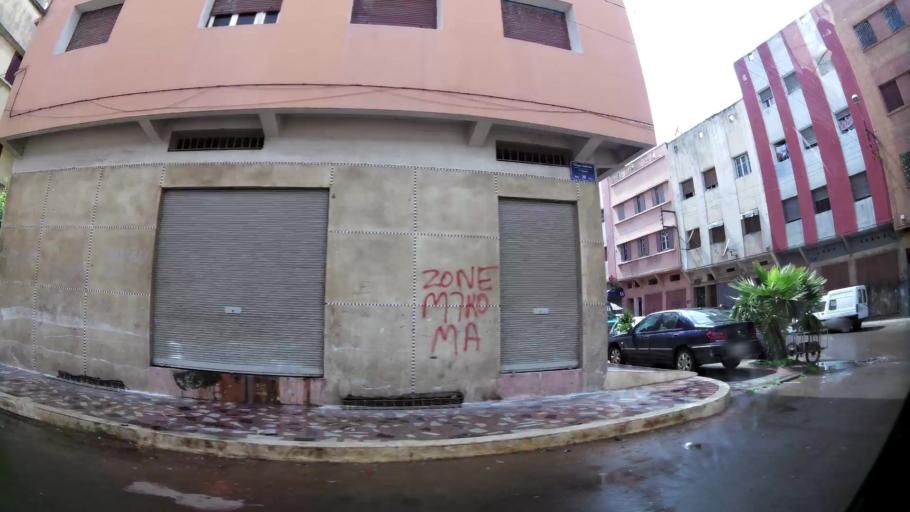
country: MA
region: Grand Casablanca
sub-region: Casablanca
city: Casablanca
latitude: 33.5408
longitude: -7.5687
